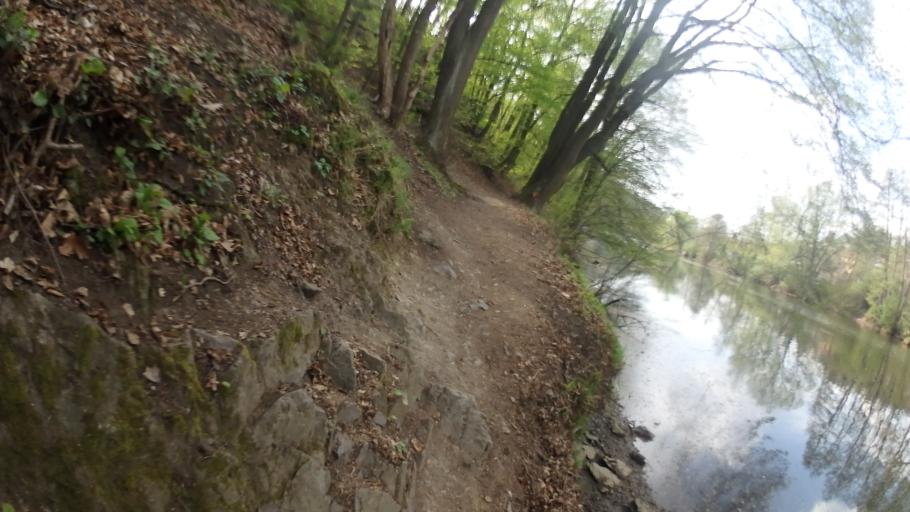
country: CZ
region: South Moravian
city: Ostopovice
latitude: 49.2177
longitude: 16.5447
